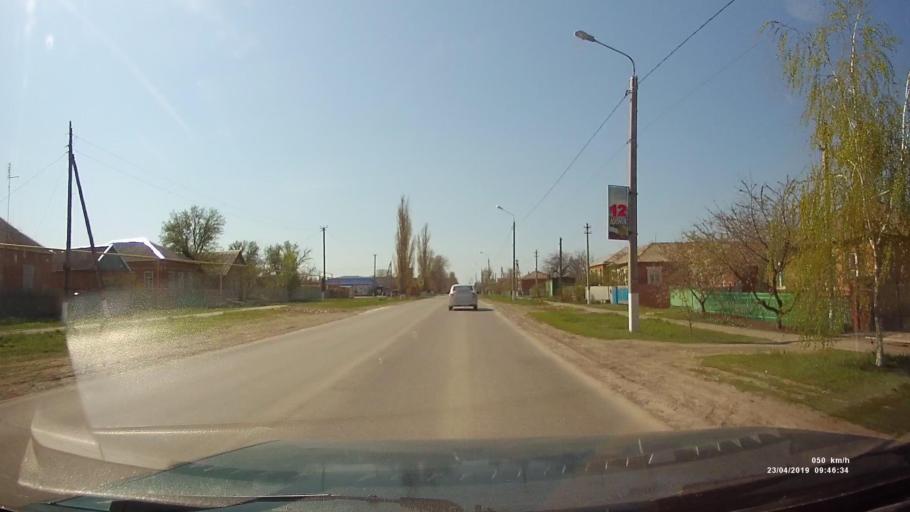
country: RU
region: Rostov
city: Orlovskiy
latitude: 46.8813
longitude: 42.0384
